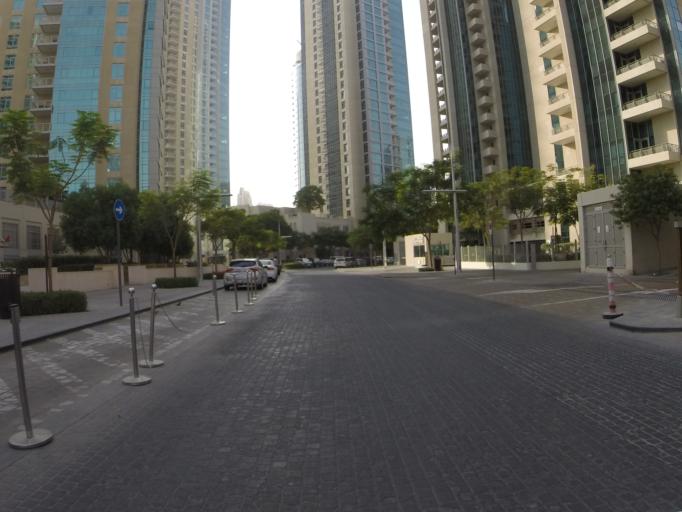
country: AE
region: Dubai
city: Dubai
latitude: 25.1921
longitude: 55.2732
